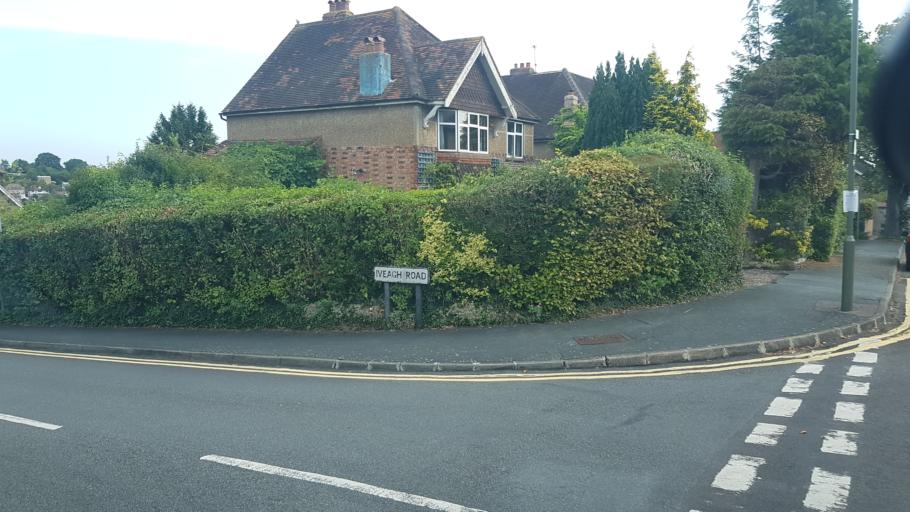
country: GB
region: England
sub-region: Surrey
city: Guildford
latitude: 51.2352
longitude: -0.5888
